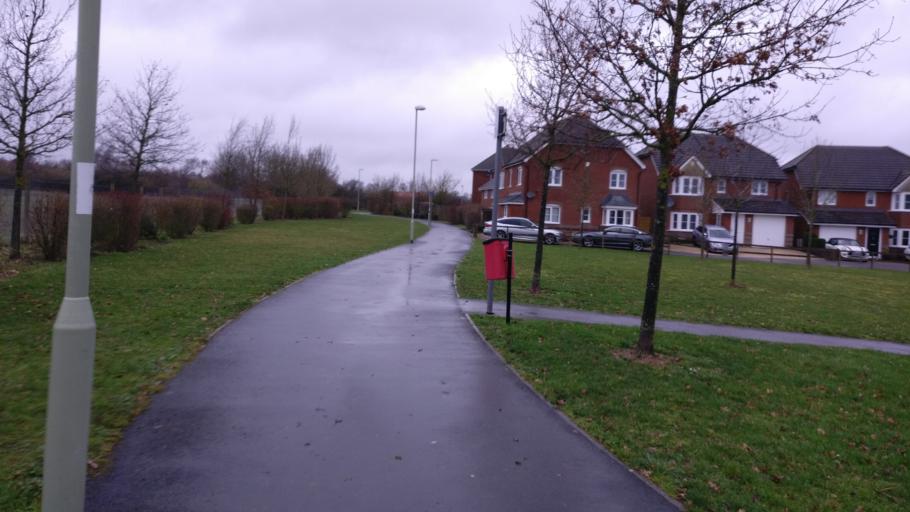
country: GB
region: England
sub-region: Hampshire
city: Basingstoke
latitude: 51.2580
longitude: -1.1416
